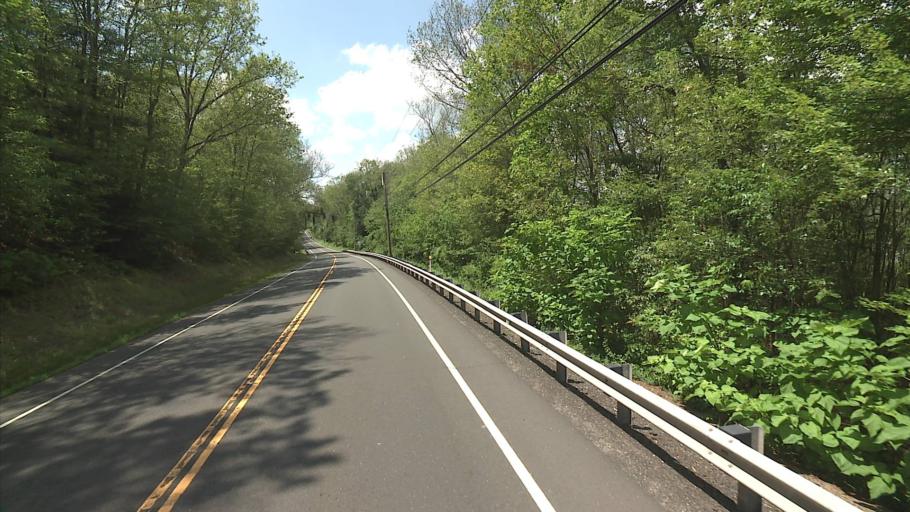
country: US
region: Connecticut
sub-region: Middlesex County
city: Higganum
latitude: 41.4956
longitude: -72.5338
